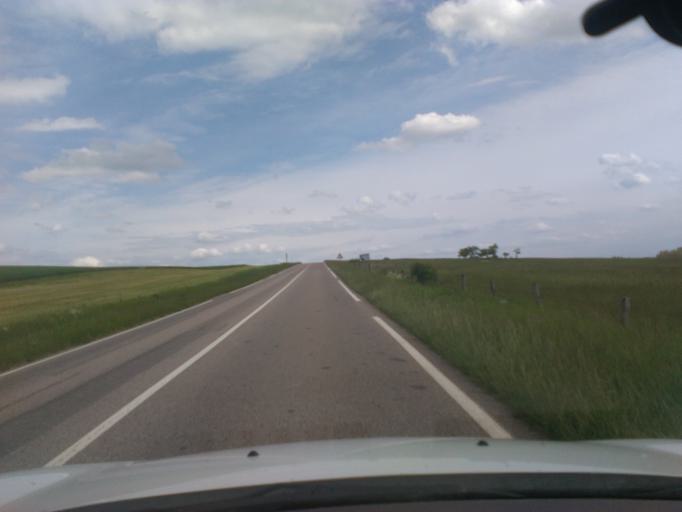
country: FR
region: Lorraine
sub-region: Departement des Vosges
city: Mirecourt
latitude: 48.2770
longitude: 6.1407
